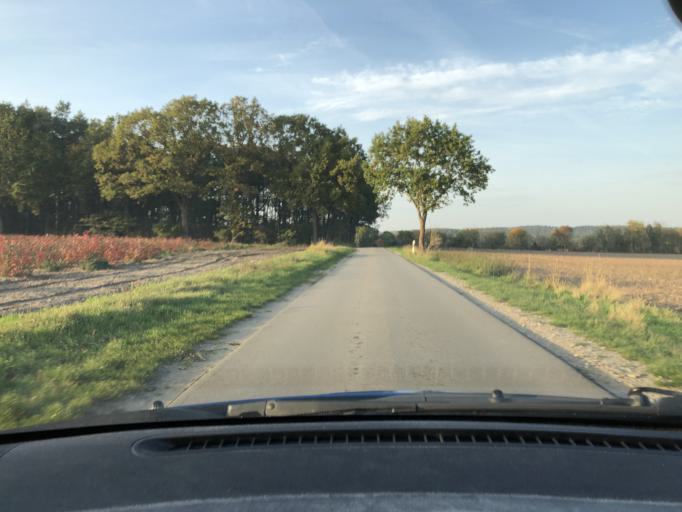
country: DE
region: Lower Saxony
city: Hitzacker
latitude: 53.1402
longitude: 11.0069
